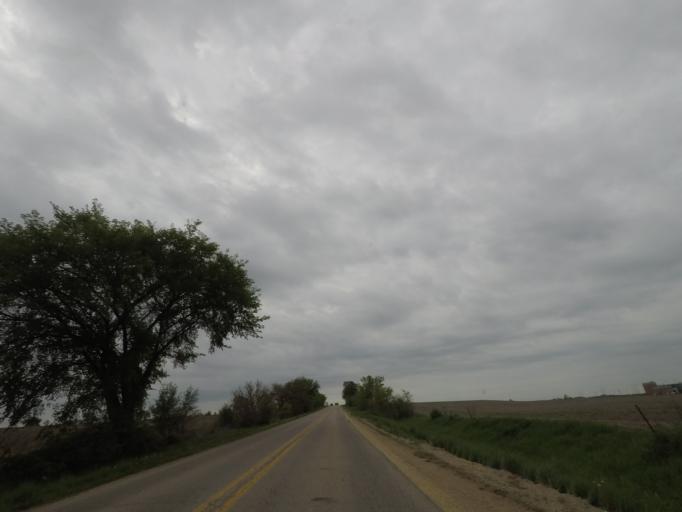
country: US
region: Illinois
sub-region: Winnebago County
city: Roscoe
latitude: 42.4488
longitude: -88.9897
